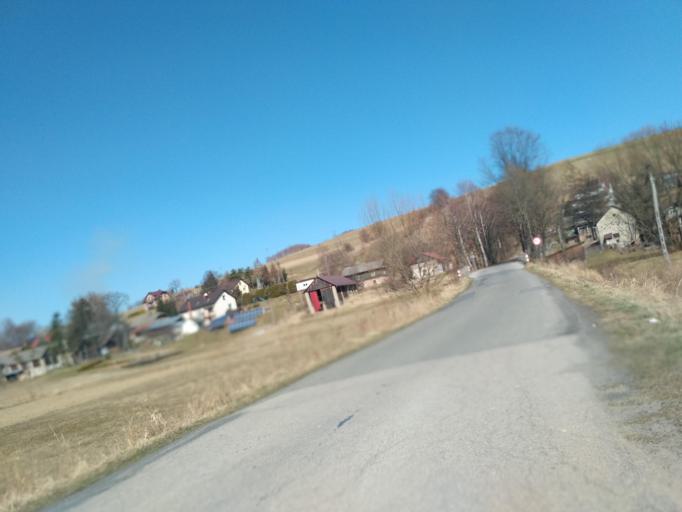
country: PL
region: Subcarpathian Voivodeship
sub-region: Powiat ropczycko-sedziszowski
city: Wielopole Skrzynskie
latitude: 49.9586
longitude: 21.5824
